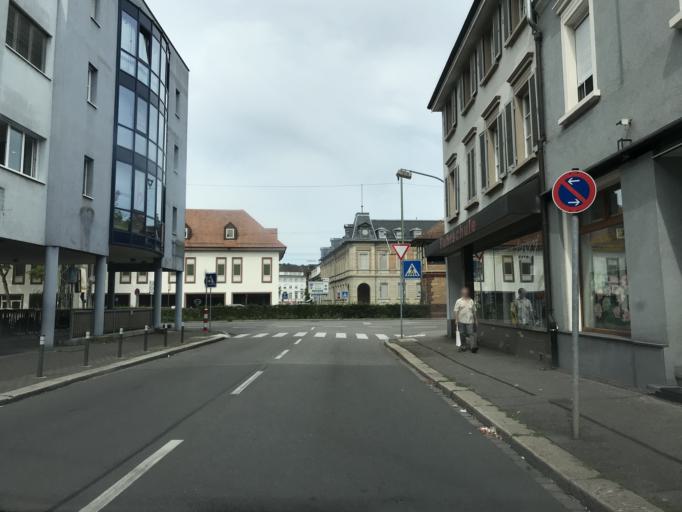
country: DE
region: Baden-Wuerttemberg
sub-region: Freiburg Region
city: Loerrach
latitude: 47.6108
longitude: 7.6640
